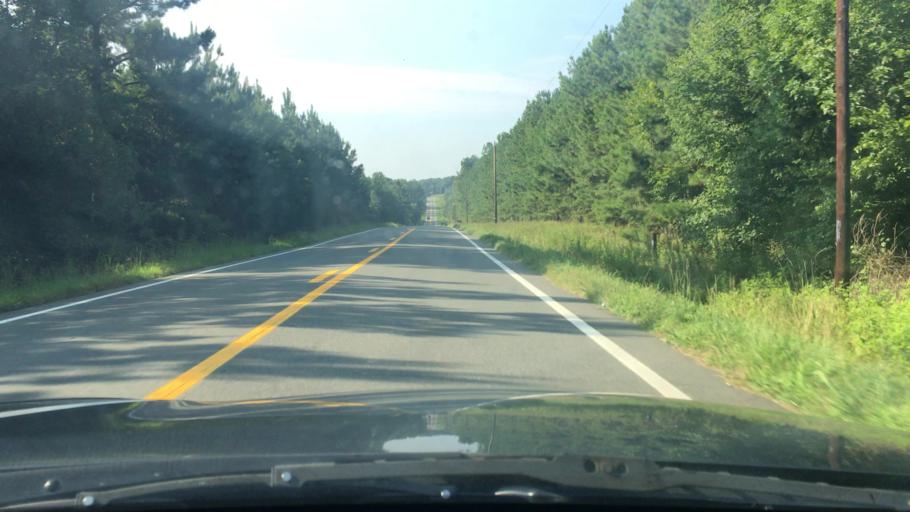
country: US
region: North Carolina
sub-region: Alamance County
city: Green Level
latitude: 36.2395
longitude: -79.3226
